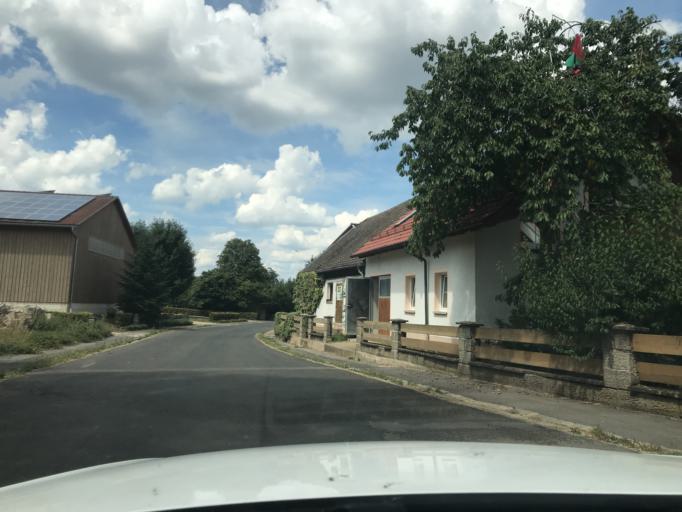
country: DE
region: Bavaria
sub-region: Upper Palatinate
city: Auerbach
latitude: 49.7418
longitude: 11.6360
